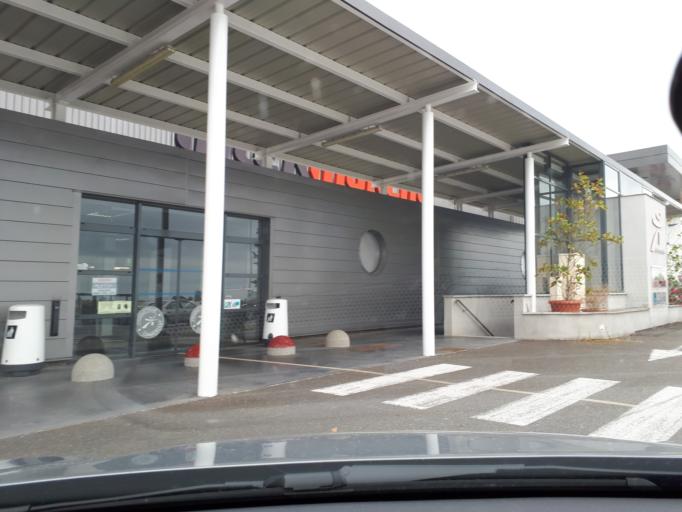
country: FR
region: Midi-Pyrenees
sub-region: Departement du Gers
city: Lectoure
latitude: 43.9355
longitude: 0.6429
